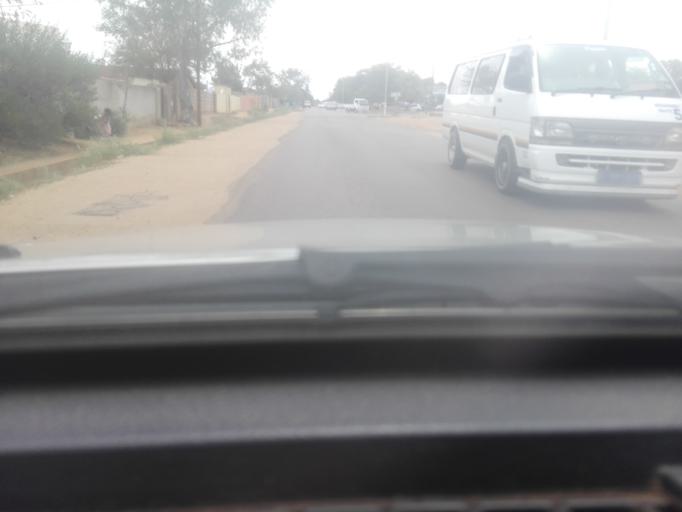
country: BW
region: South East
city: Gaborone
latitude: -24.6221
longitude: 25.9424
